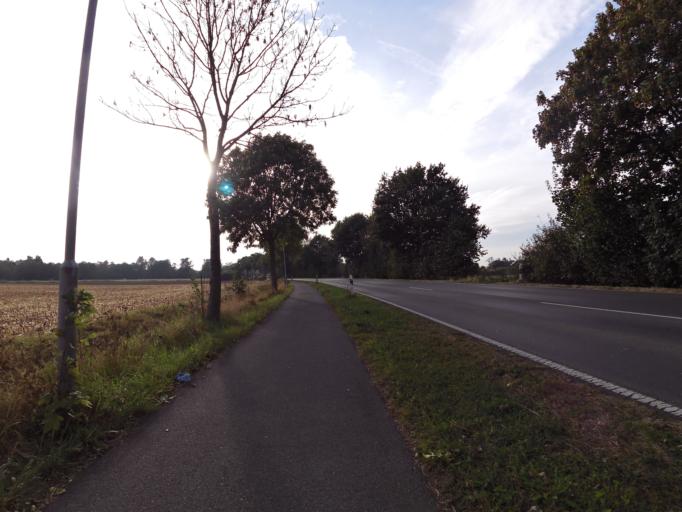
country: DE
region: North Rhine-Westphalia
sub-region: Regierungsbezirk Dusseldorf
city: Bocholt
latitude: 51.8161
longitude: 6.5857
